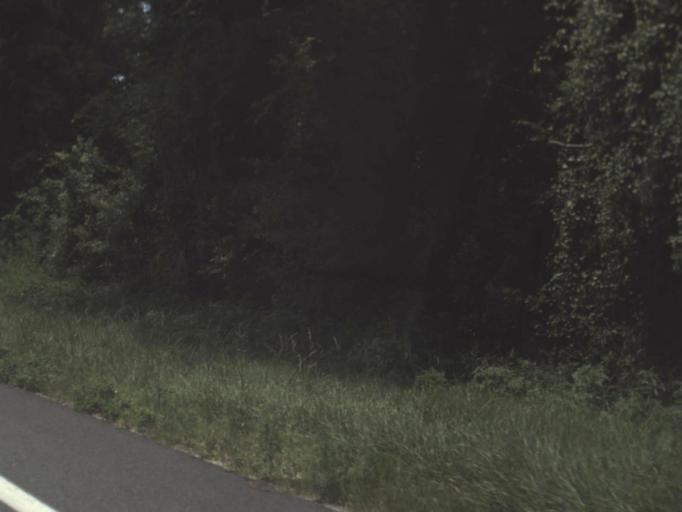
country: US
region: Florida
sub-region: Suwannee County
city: Wellborn
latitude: 30.3800
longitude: -82.8121
